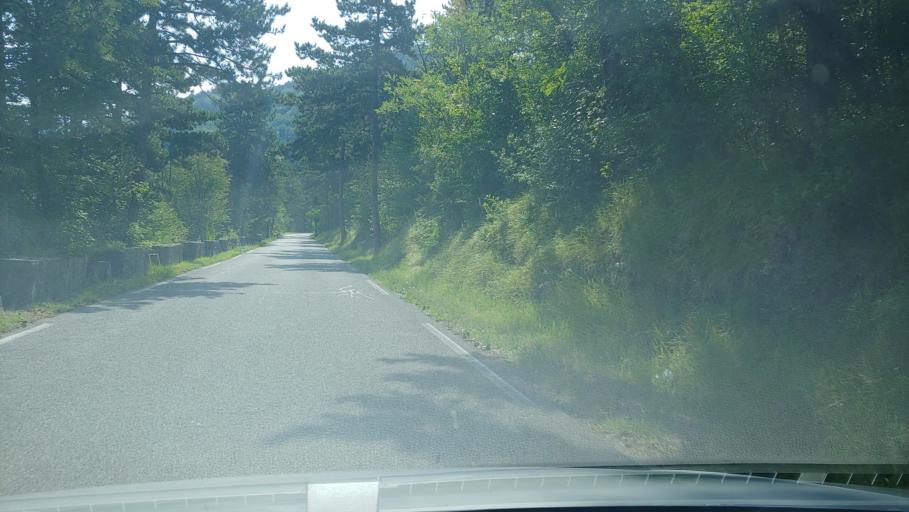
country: SI
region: Komen
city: Komen
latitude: 45.8499
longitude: 13.7854
